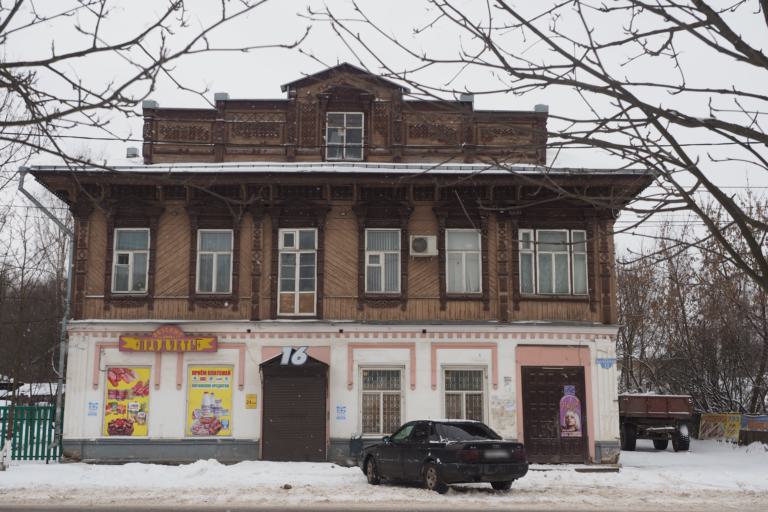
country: RU
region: Tverskaya
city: Bezhetsk
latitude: 57.7873
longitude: 36.6911
